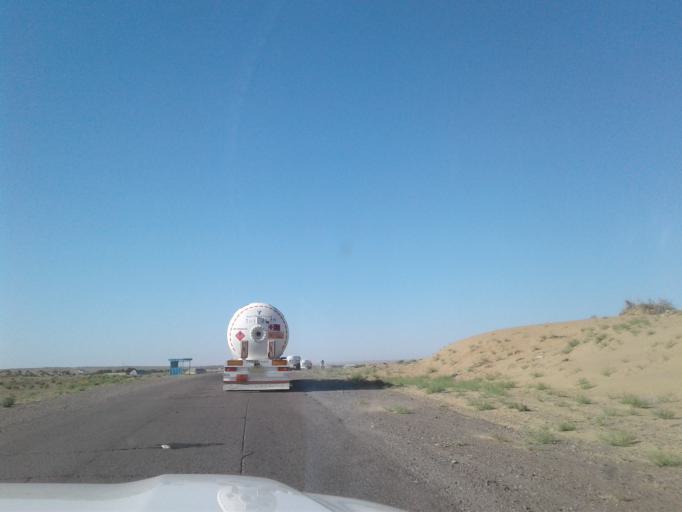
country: TM
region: Mary
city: Yoloeten
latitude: 36.7704
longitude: 62.4806
